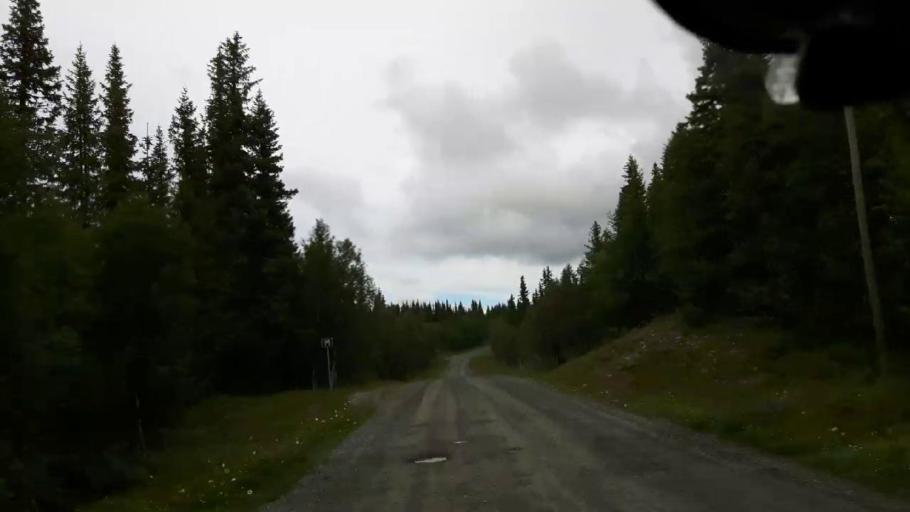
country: SE
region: Jaemtland
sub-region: Krokoms Kommun
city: Valla
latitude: 63.7572
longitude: 13.8374
